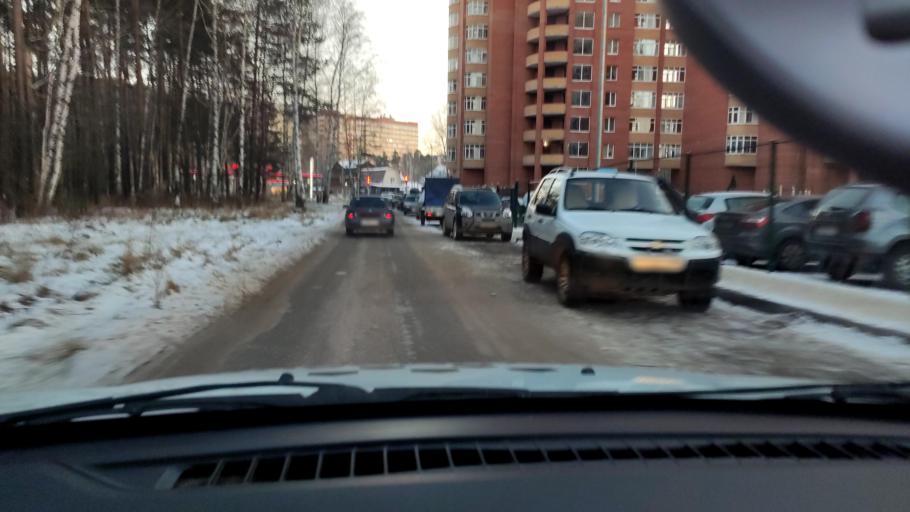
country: RU
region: Perm
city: Kondratovo
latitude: 58.0335
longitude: 56.0147
